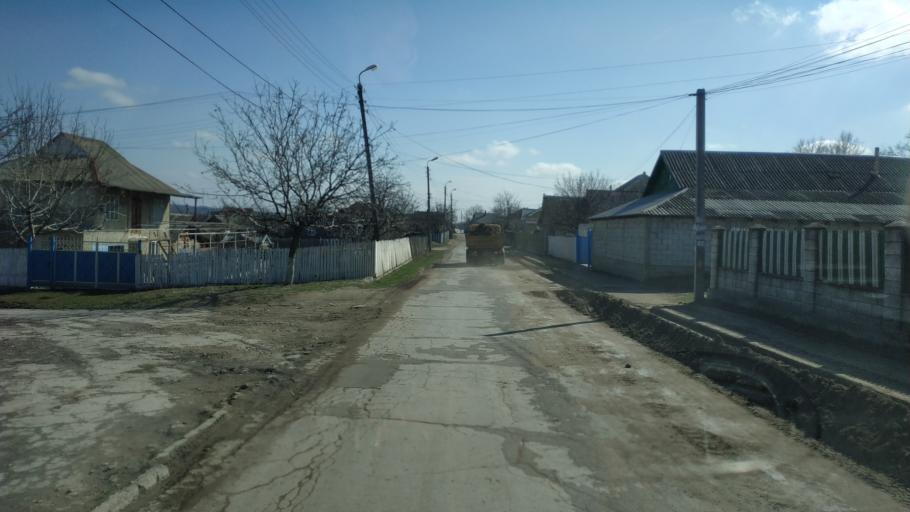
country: MD
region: Hincesti
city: Hincesti
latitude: 46.9323
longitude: 28.6466
